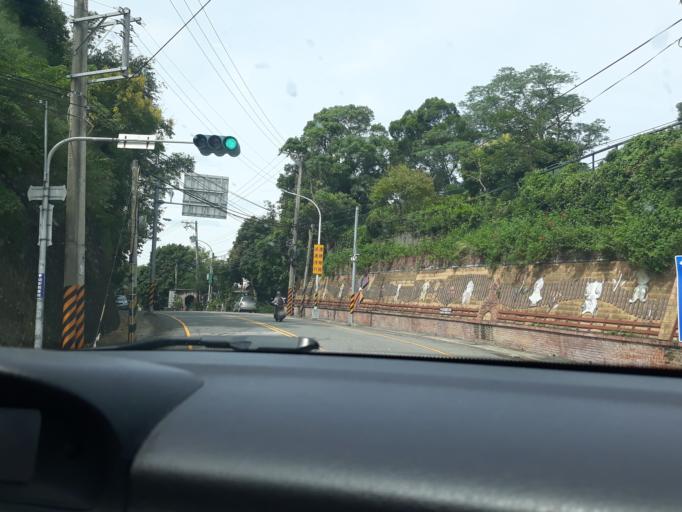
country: TW
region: Taiwan
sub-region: Miaoli
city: Miaoli
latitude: 24.5544
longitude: 120.8080
